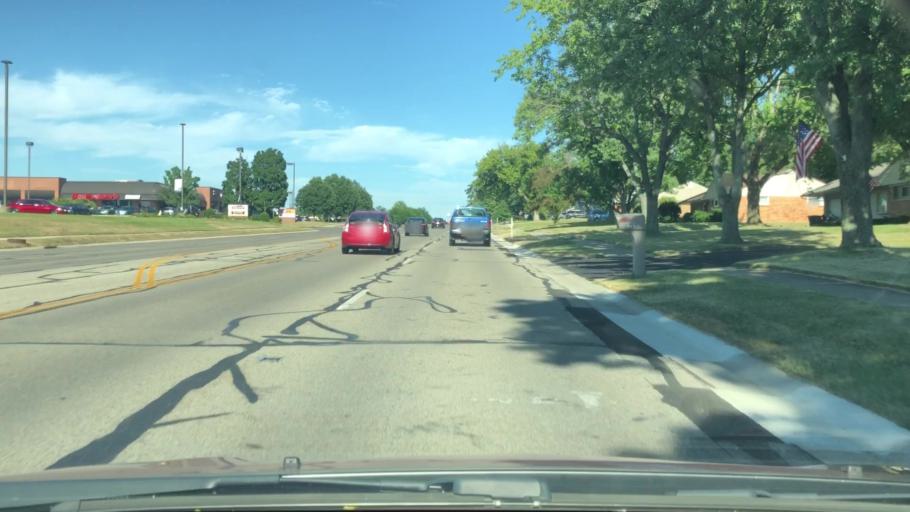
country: US
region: Ohio
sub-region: Montgomery County
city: Centerville
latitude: 39.6438
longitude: -84.1529
